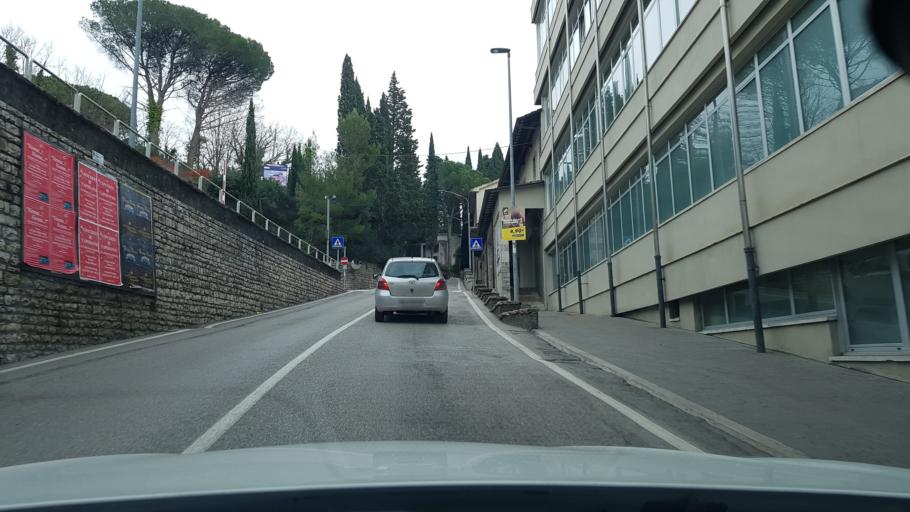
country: IT
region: Umbria
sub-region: Provincia di Perugia
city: Perugia
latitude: 43.1198
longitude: 12.3667
